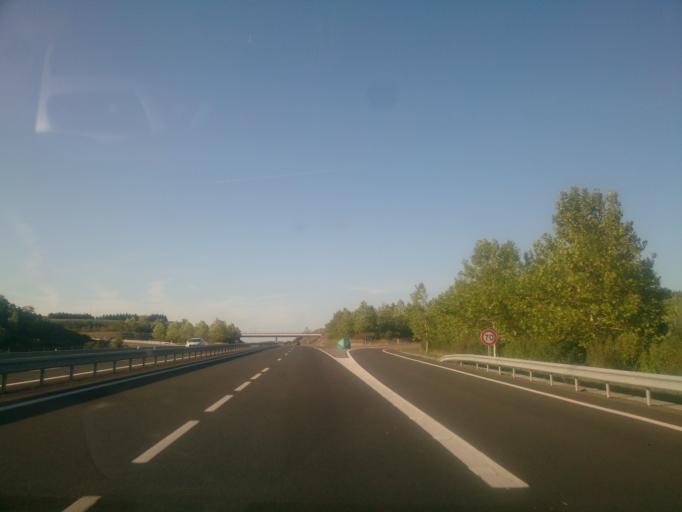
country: FR
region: Midi-Pyrenees
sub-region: Departement du Lot
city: Cahors
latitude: 44.5274
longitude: 1.5118
